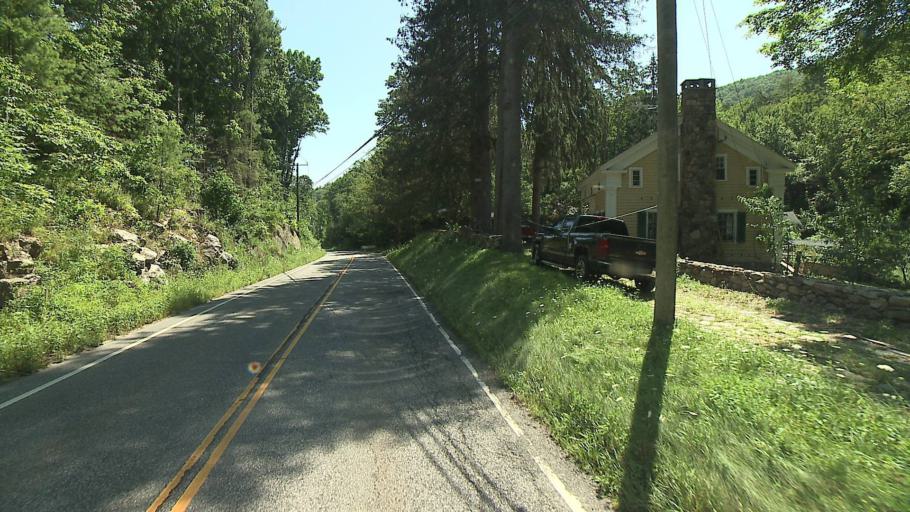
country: US
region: Connecticut
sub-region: Litchfield County
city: Kent
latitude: 41.8224
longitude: -73.3958
